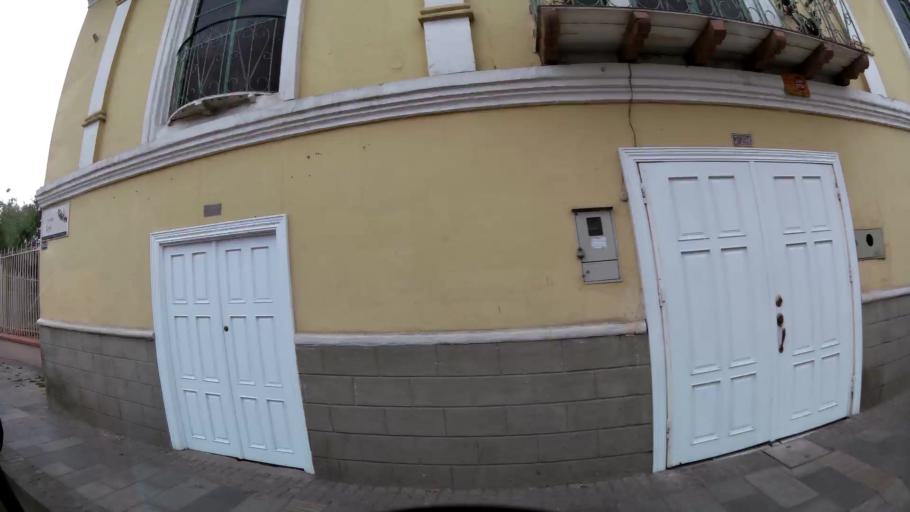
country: EC
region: Azuay
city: Cuenca
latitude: -2.9022
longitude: -79.0182
